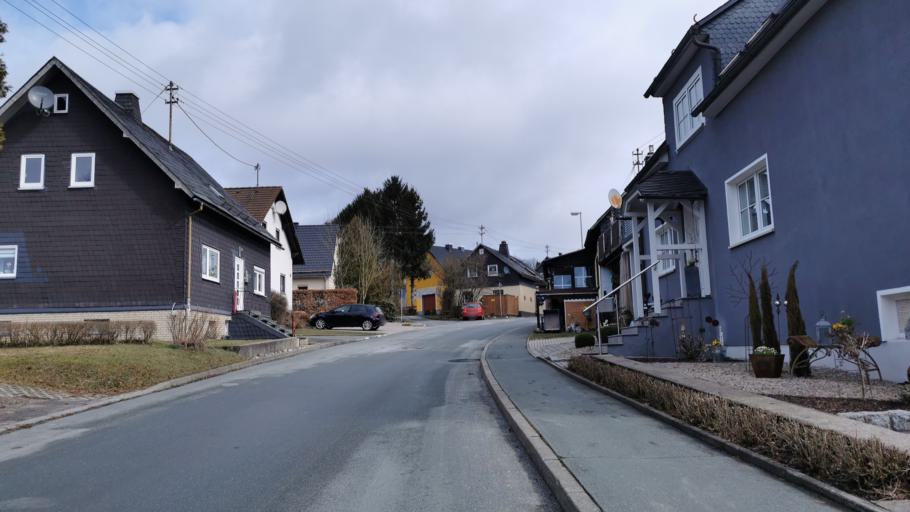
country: DE
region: Bavaria
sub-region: Upper Franconia
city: Reichenbach
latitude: 50.4264
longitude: 11.4154
